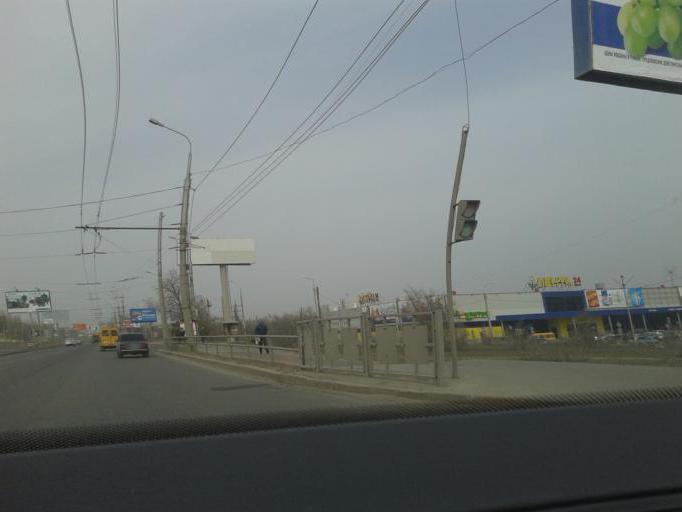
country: RU
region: Volgograd
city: Volgograd
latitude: 48.6403
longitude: 44.4317
